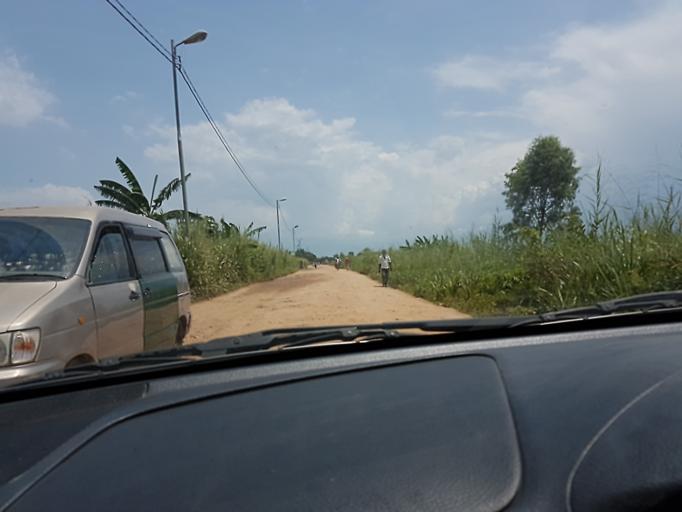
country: CD
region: South Kivu
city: Uvira
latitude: -3.3393
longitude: 29.2072
